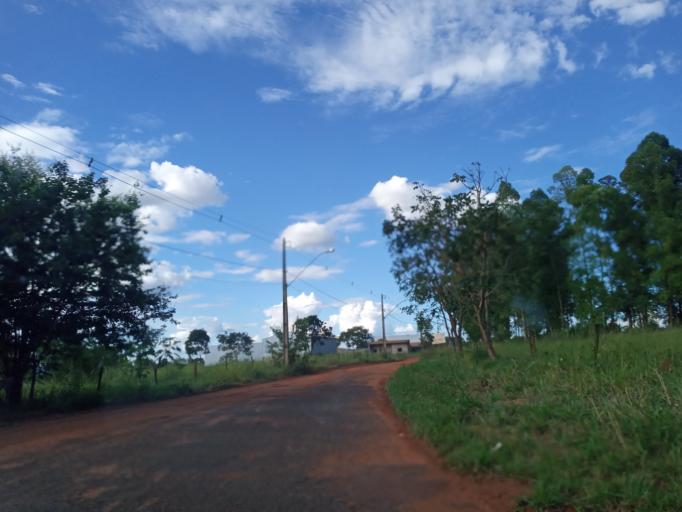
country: BR
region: Minas Gerais
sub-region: Ituiutaba
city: Ituiutaba
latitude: -18.9600
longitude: -49.4916
